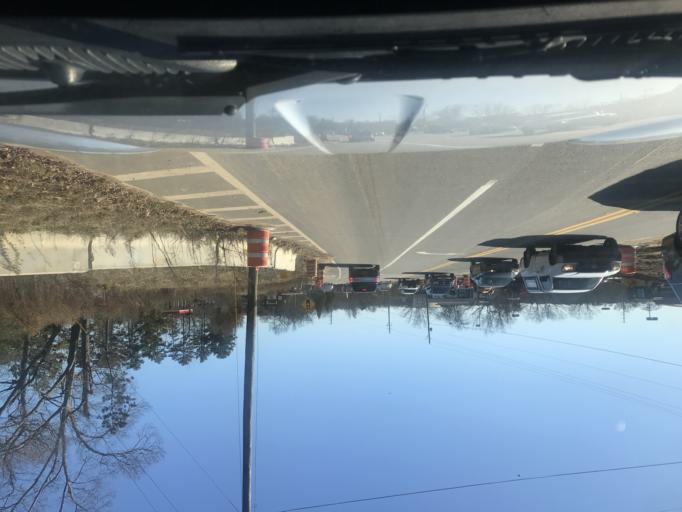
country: US
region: Georgia
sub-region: Barrow County
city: Winder
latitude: 33.9452
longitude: -83.7559
